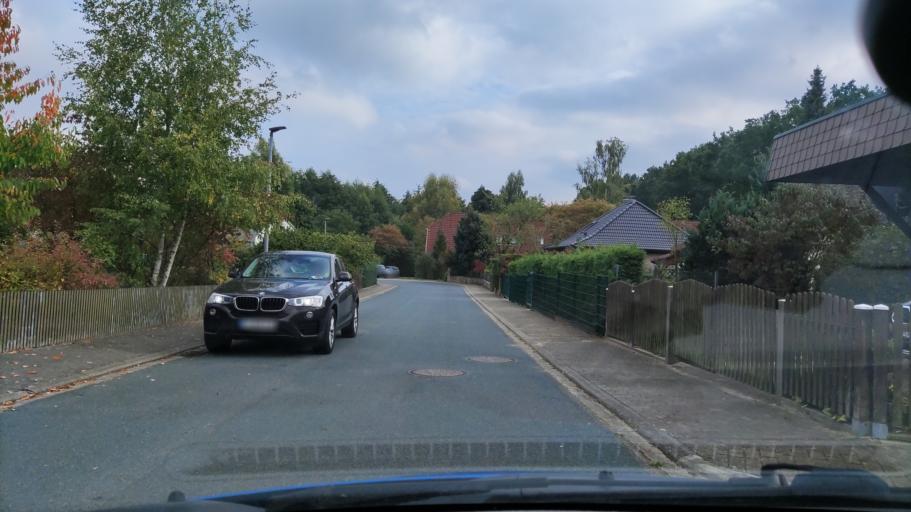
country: DE
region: Lower Saxony
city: Hitzacker
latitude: 53.1498
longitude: 11.0253
